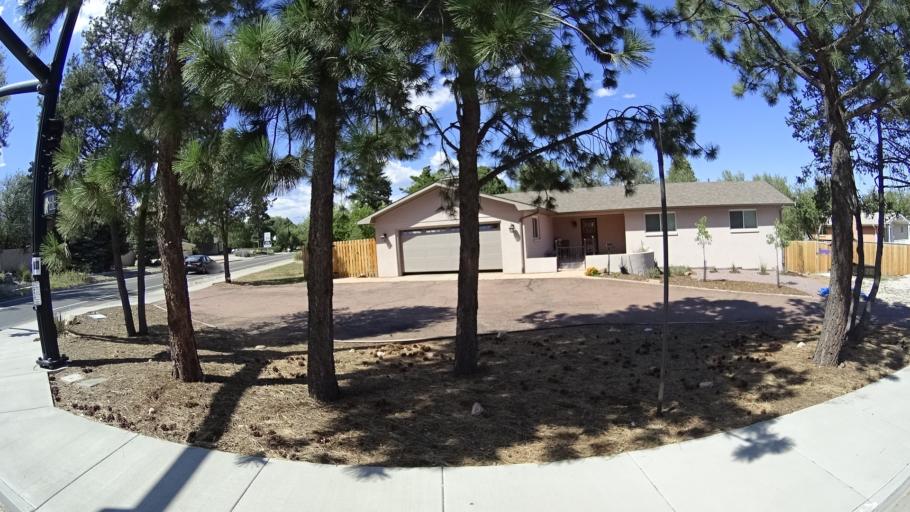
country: US
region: Colorado
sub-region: El Paso County
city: Colorado Springs
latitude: 38.8127
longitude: -104.8582
